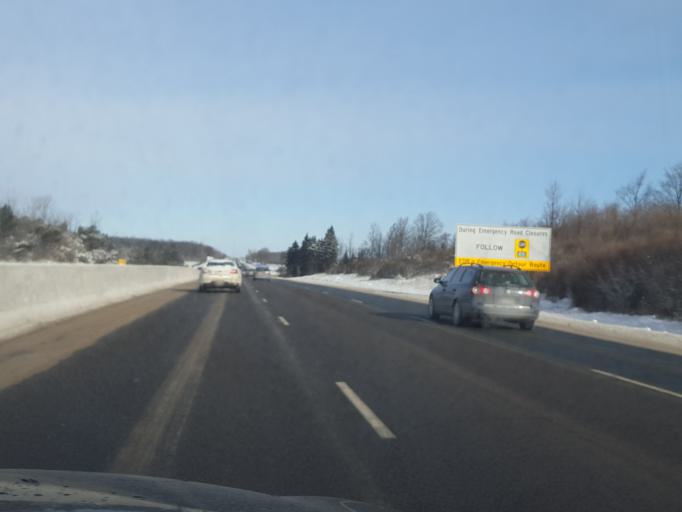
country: CA
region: Ontario
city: Innisfil
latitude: 44.2557
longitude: -79.6718
